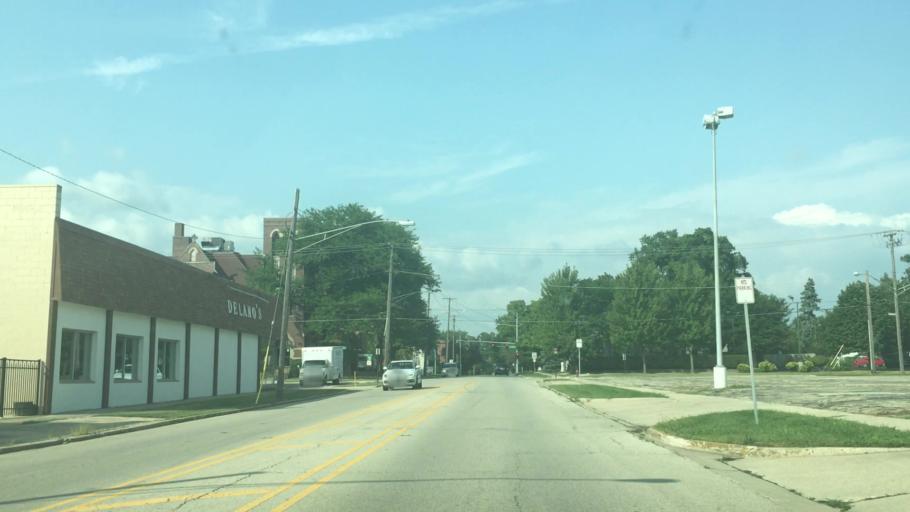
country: US
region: Illinois
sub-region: DeKalb County
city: DeKalb
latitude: 41.9308
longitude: -88.7493
